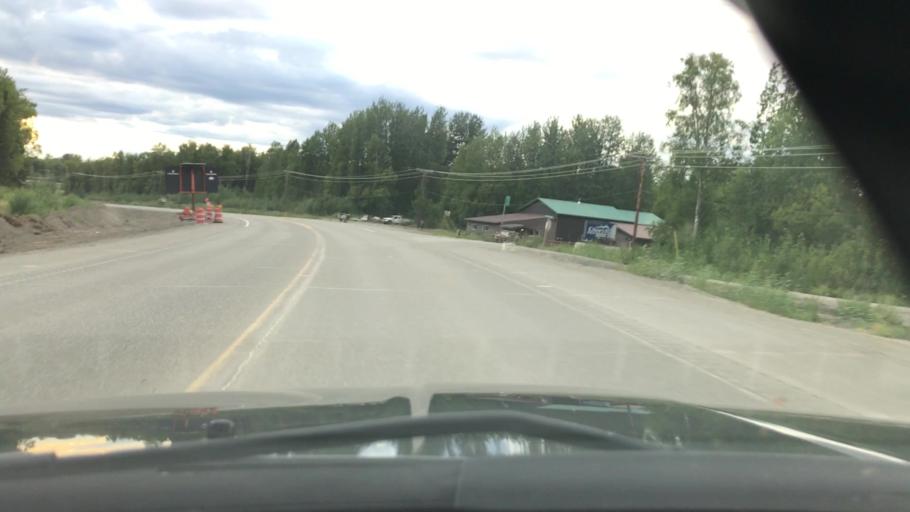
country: US
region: Alaska
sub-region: Matanuska-Susitna Borough
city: Y
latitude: 62.1378
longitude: -150.0443
